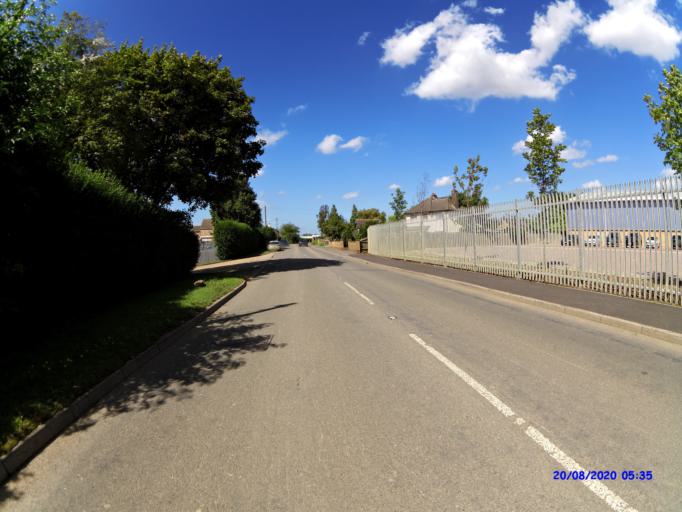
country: GB
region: England
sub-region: Cambridgeshire
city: Whittlesey
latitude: 52.5458
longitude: -0.1143
